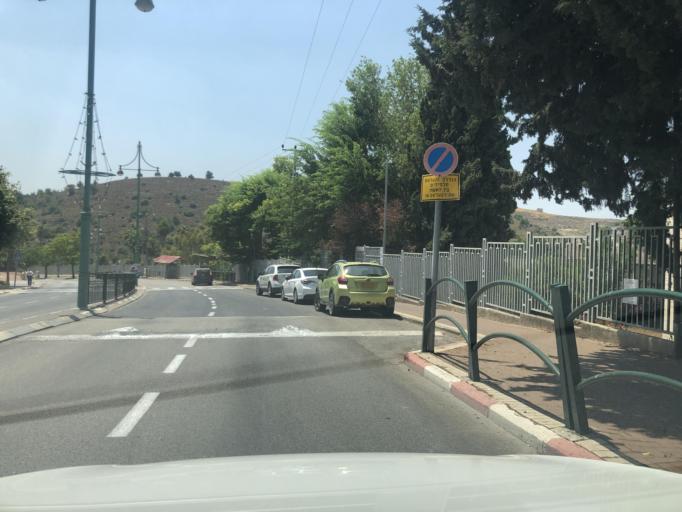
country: IL
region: Haifa
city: Daliyat el Karmil
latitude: 32.6544
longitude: 35.1051
